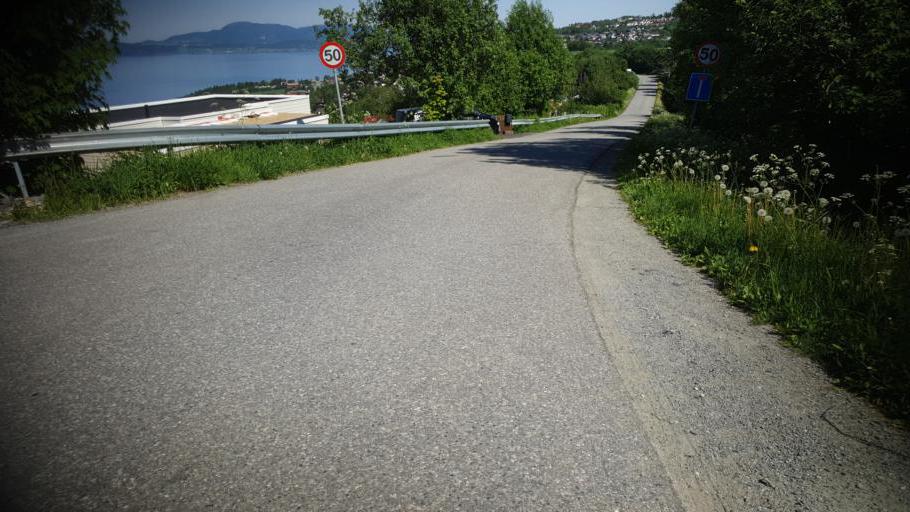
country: NO
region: Sor-Trondelag
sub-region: Malvik
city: Malvik
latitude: 63.4311
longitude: 10.6058
